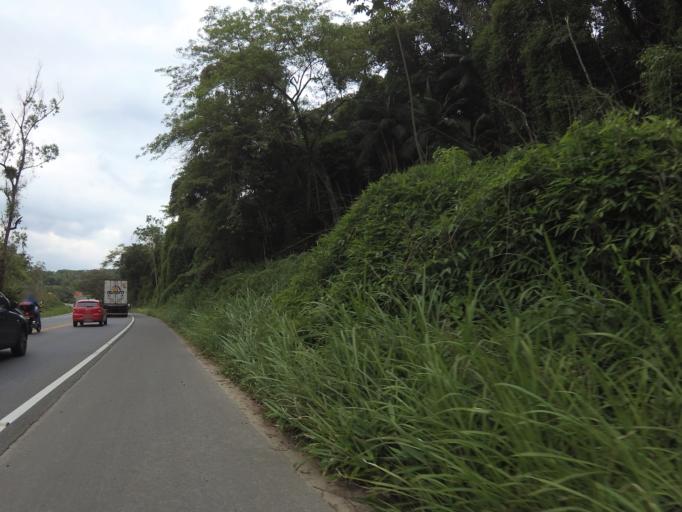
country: BR
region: Santa Catarina
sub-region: Indaial
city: Indaial
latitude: -26.8393
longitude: -49.1646
